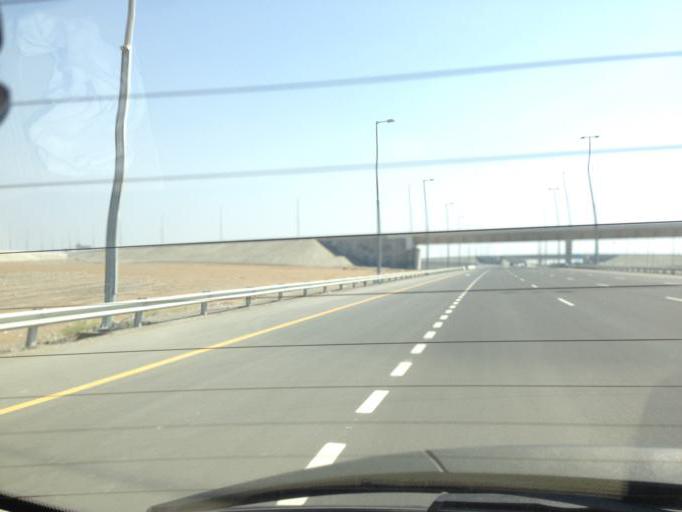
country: OM
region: Al Batinah
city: Barka'
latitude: 23.5744
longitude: 57.7263
